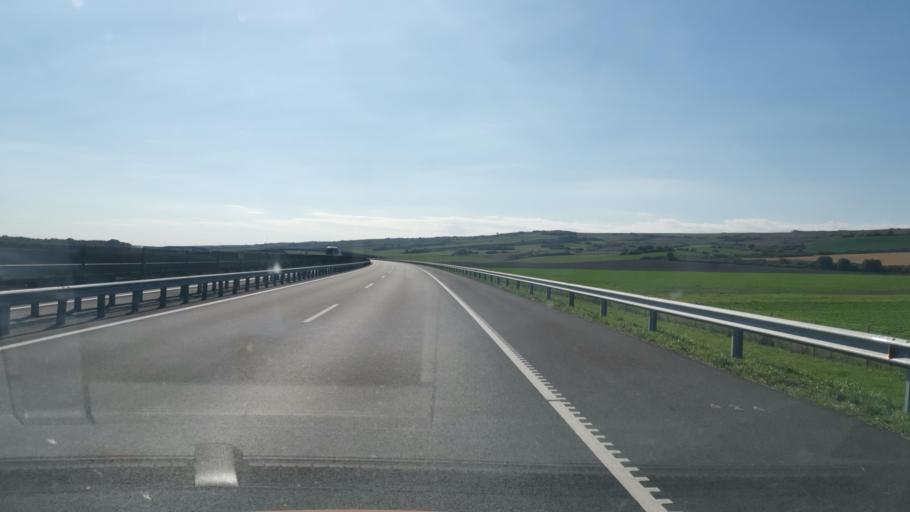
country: HU
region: Borsod-Abauj-Zemplen
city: Szikszo
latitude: 48.2019
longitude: 20.9086
